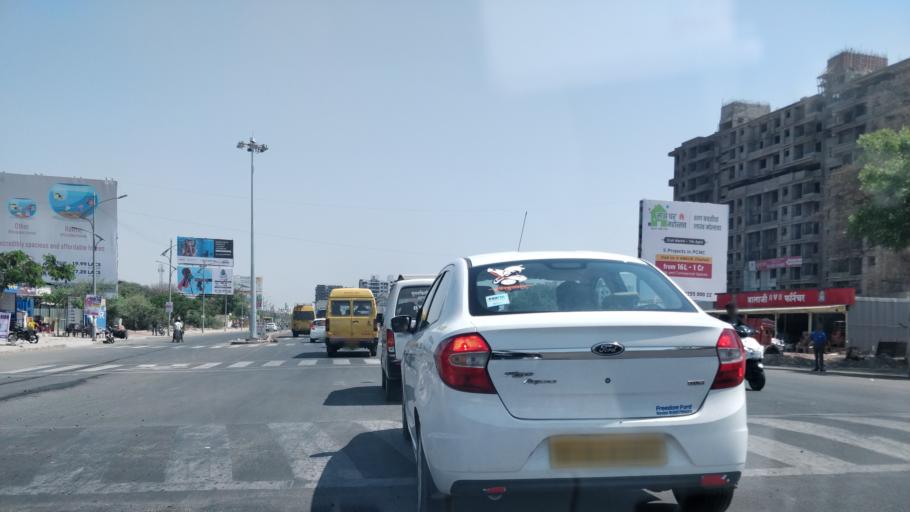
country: IN
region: Maharashtra
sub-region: Pune Division
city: Alandi
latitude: 18.6571
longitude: 73.8855
